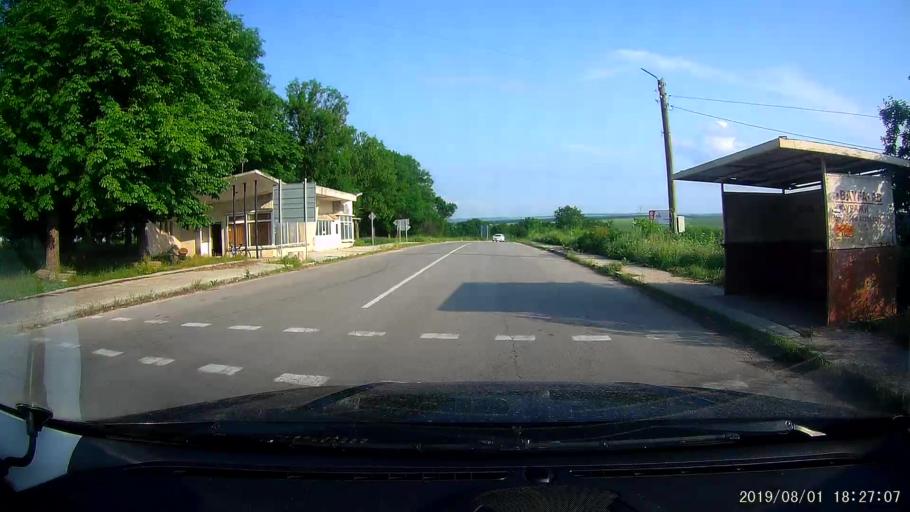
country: BG
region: Shumen
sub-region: Obshtina Venets
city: Venets
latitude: 43.5918
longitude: 26.9832
